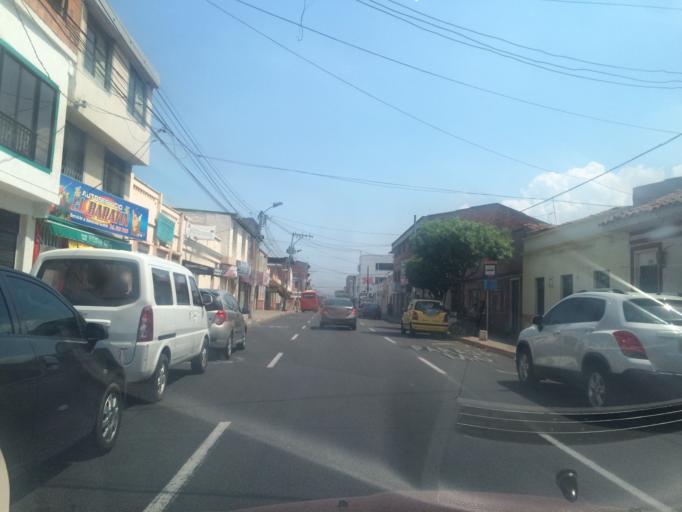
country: CO
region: Valle del Cauca
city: Cali
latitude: 3.4392
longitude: -76.5347
